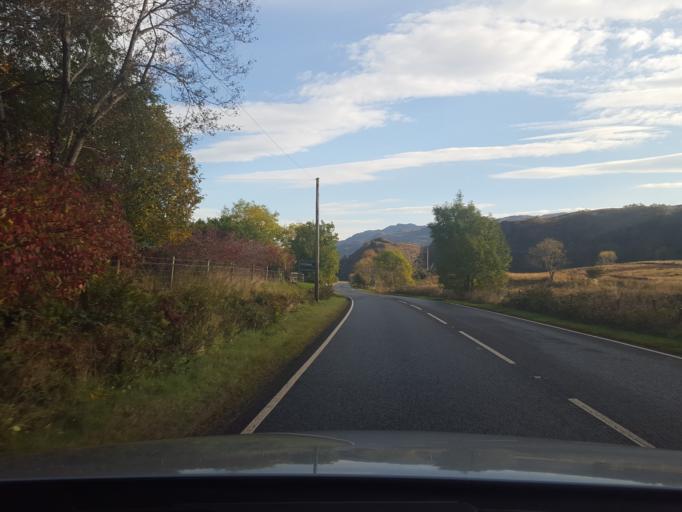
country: GB
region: Scotland
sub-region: Highland
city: Fort William
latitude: 57.2849
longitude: -5.5577
